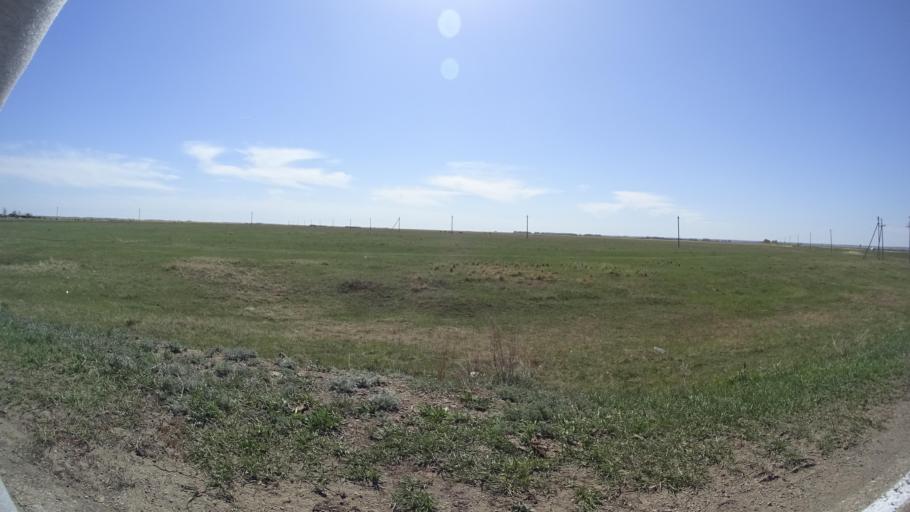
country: RU
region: Chelyabinsk
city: Chesma
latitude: 53.8033
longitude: 61.0129
